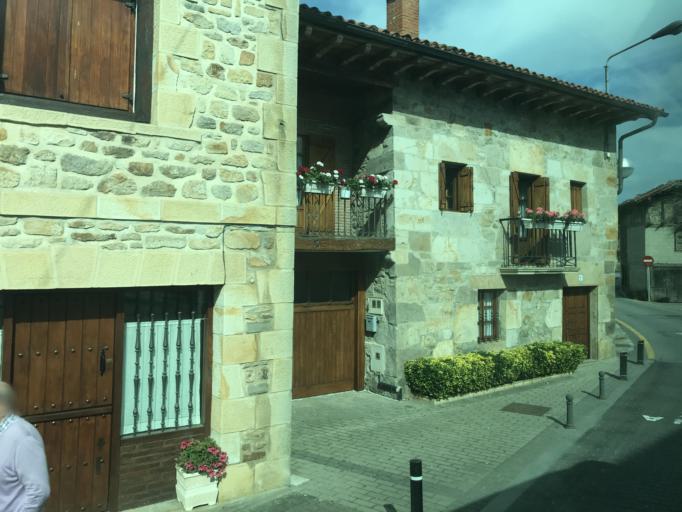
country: ES
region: Basque Country
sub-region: Bizkaia
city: Otxandio
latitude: 43.0418
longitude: -2.6540
